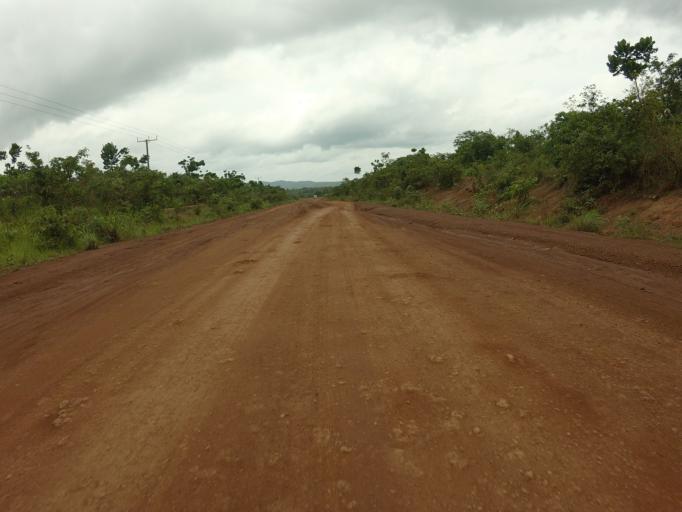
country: GH
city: Kpandae
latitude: 8.3028
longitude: 0.4857
